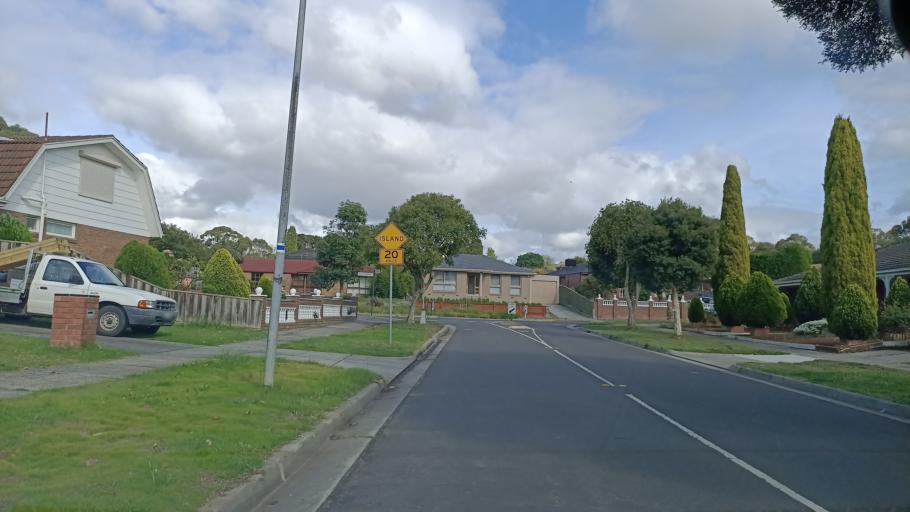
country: AU
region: Victoria
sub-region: Monash
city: Mulgrave
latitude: -37.9251
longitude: 145.2022
